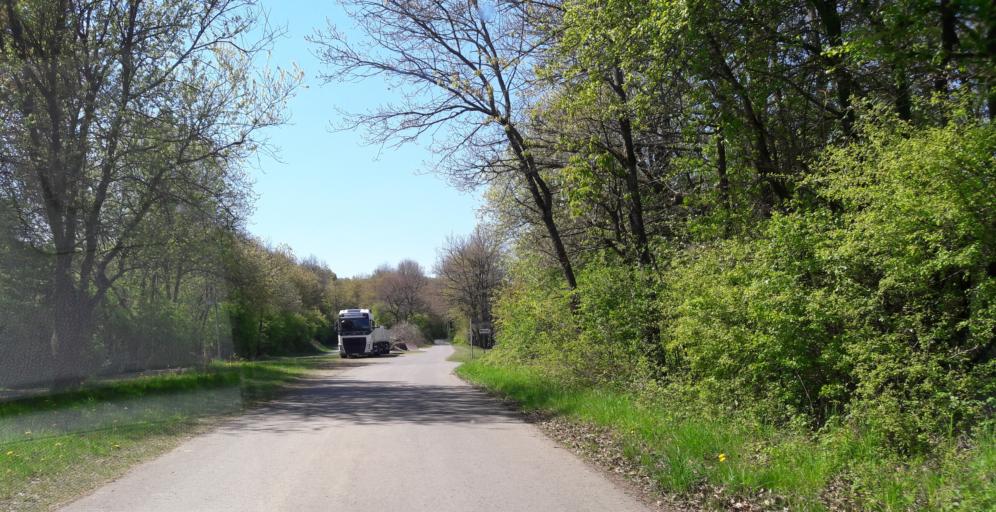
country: DE
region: Rheinland-Pfalz
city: Pfeffelbach
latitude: 49.5374
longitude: 7.3314
